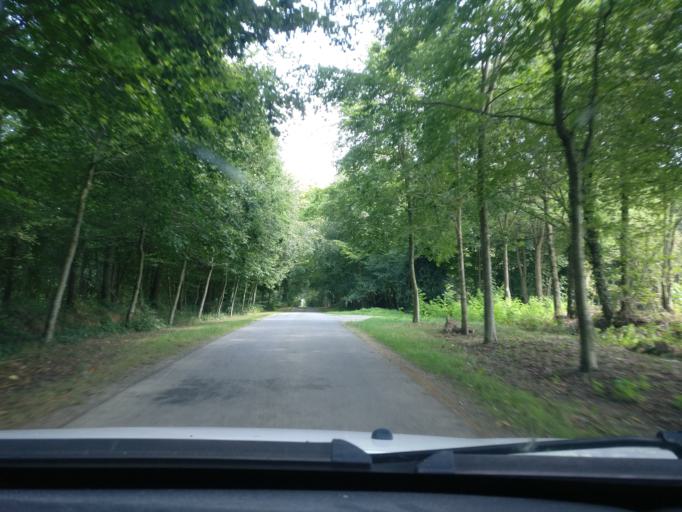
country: FR
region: Brittany
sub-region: Departement d'Ille-et-Vilaine
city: Erce-pres-Liffre
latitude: 48.2600
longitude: -1.5102
